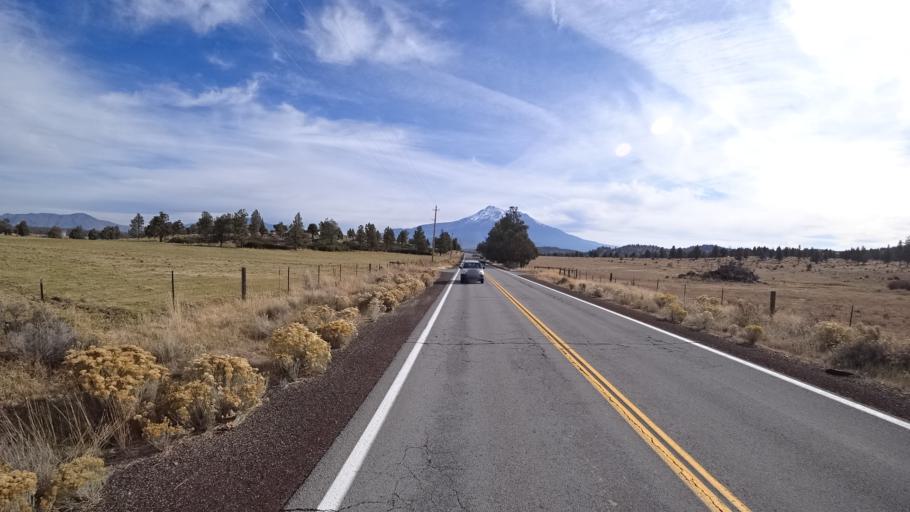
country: US
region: California
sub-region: Siskiyou County
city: Weed
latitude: 41.5553
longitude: -122.3850
